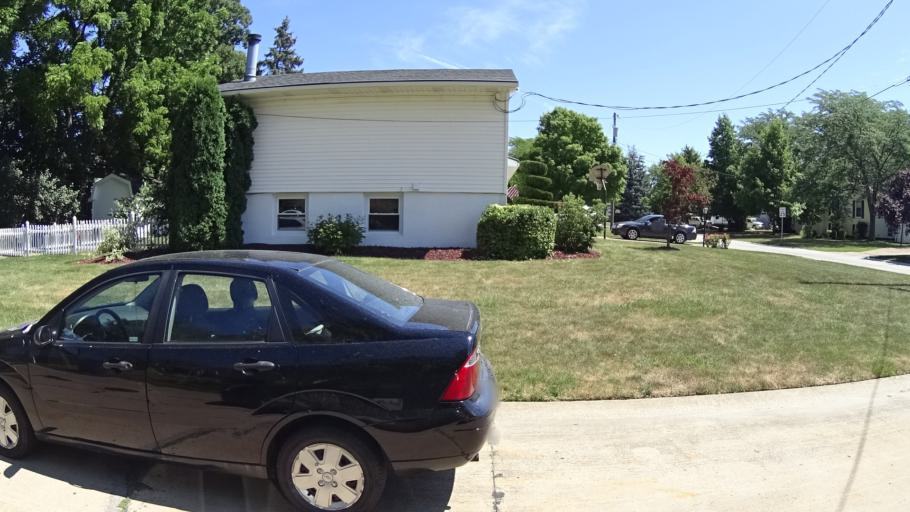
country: US
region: Ohio
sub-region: Erie County
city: Sandusky
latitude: 41.4104
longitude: -82.6934
